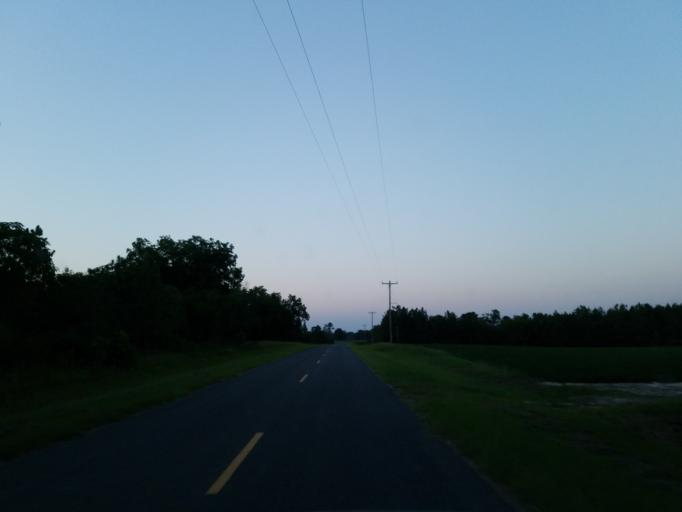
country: US
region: Georgia
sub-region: Dooly County
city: Unadilla
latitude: 32.2150
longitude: -83.7967
